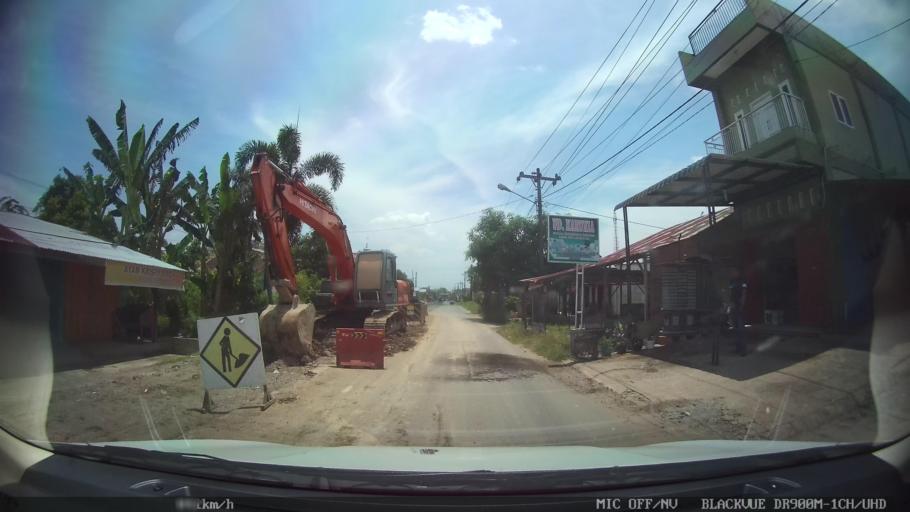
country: ID
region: North Sumatra
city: Binjai
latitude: 3.5912
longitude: 98.5000
